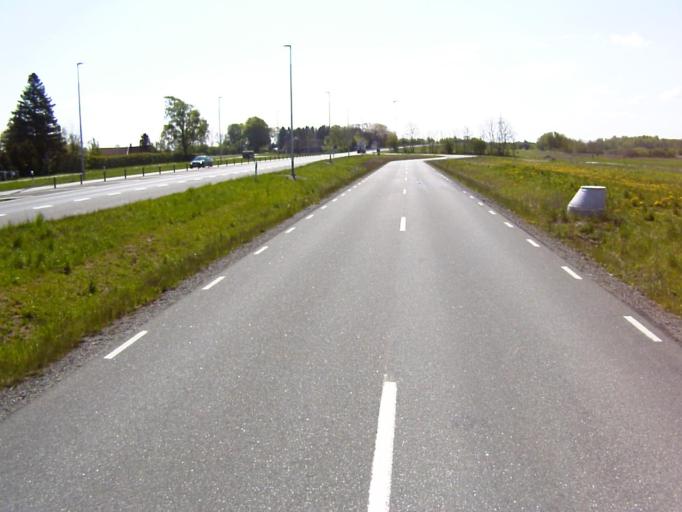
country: SE
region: Skane
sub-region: Kristianstads Kommun
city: Fjalkinge
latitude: 56.0021
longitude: 14.2655
